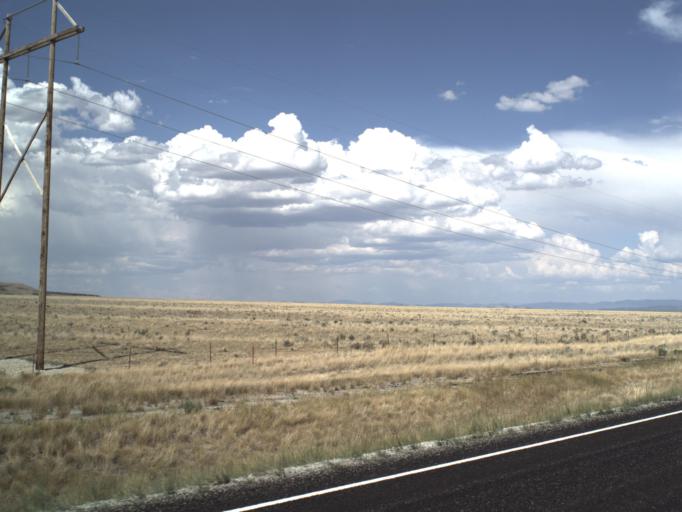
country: US
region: Idaho
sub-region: Power County
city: American Falls
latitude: 41.9692
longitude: -113.1103
